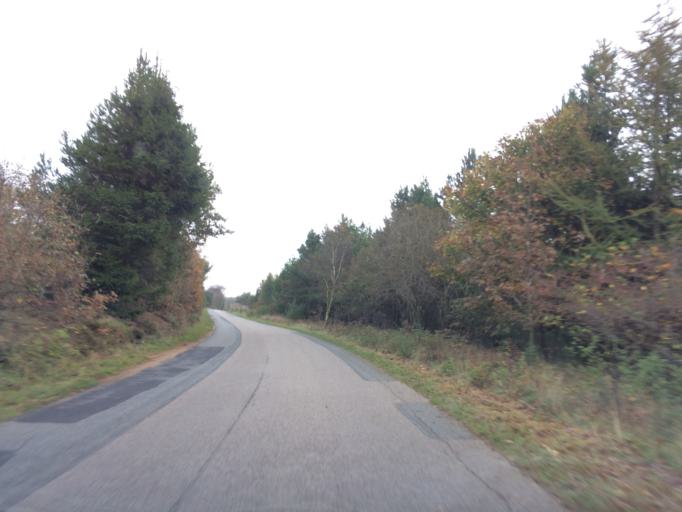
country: DK
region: Central Jutland
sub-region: Holstebro Kommune
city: Holstebro
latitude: 56.3458
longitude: 8.5069
